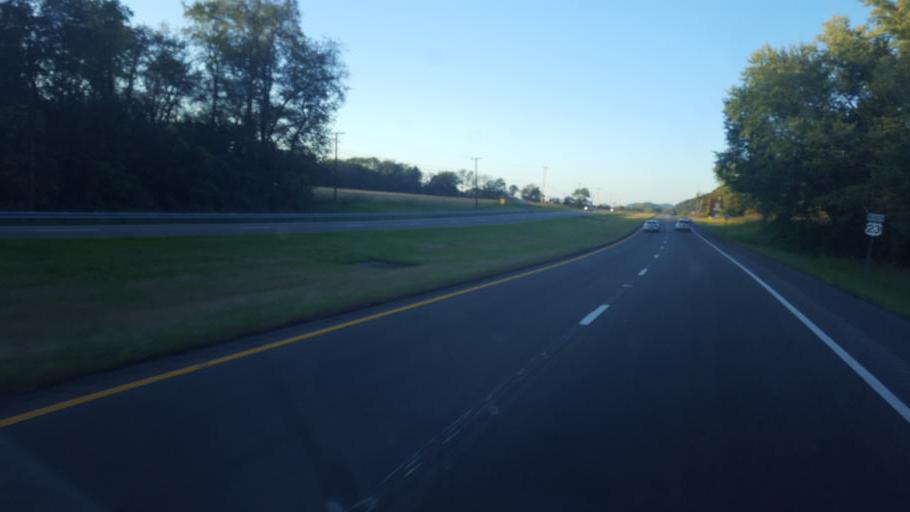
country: US
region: Ohio
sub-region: Scioto County
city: Rosemount
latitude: 38.8245
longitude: -82.9830
